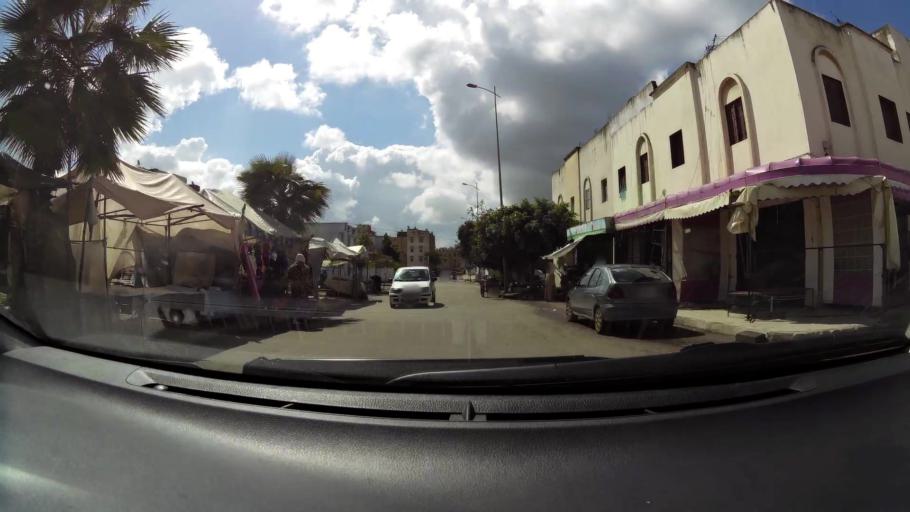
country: MA
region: Grand Casablanca
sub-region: Mediouna
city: Tit Mellil
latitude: 33.5499
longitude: -7.4864
